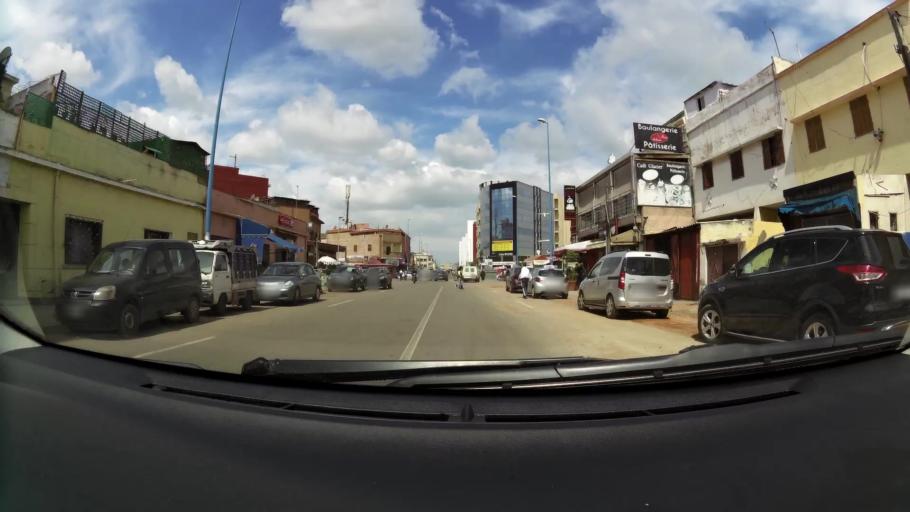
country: MA
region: Grand Casablanca
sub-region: Casablanca
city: Casablanca
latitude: 33.6164
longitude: -7.5398
